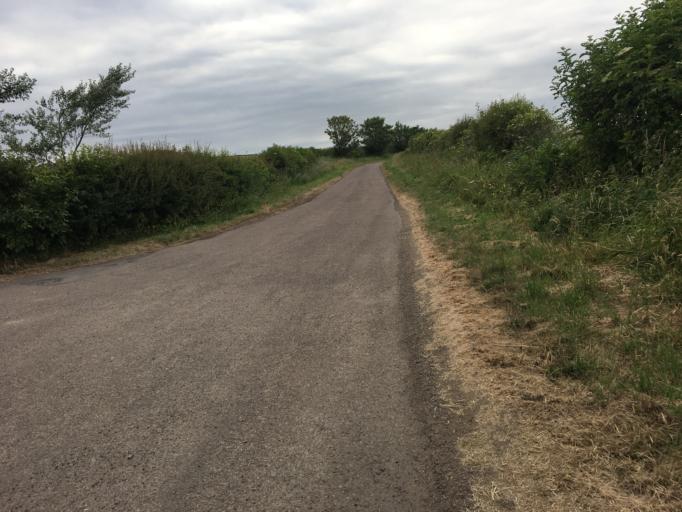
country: GB
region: England
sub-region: Northumberland
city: Lowick
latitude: 55.6551
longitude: -1.9008
